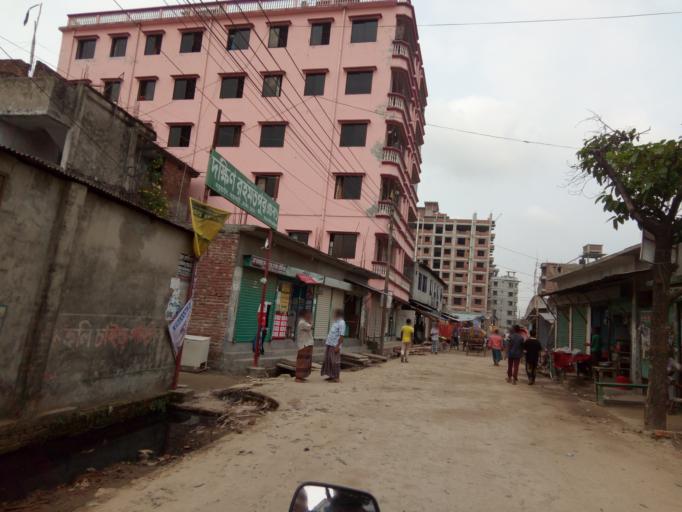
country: BD
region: Dhaka
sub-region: Dhaka
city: Dhaka
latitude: 23.7023
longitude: 90.4670
